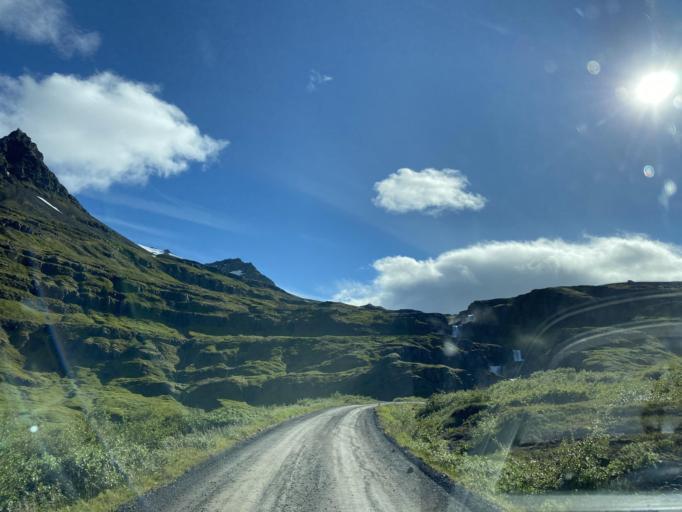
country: IS
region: East
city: Eskifjoerdur
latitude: 65.1810
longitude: -14.0763
